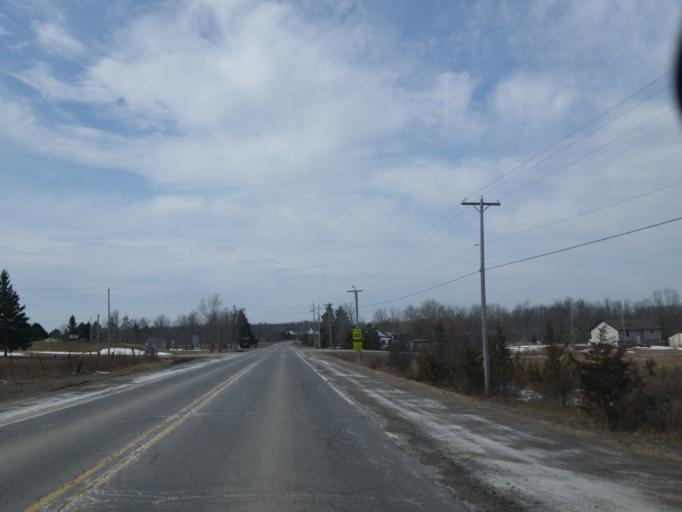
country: CA
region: Ontario
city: Deseronto
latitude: 44.1869
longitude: -77.1313
